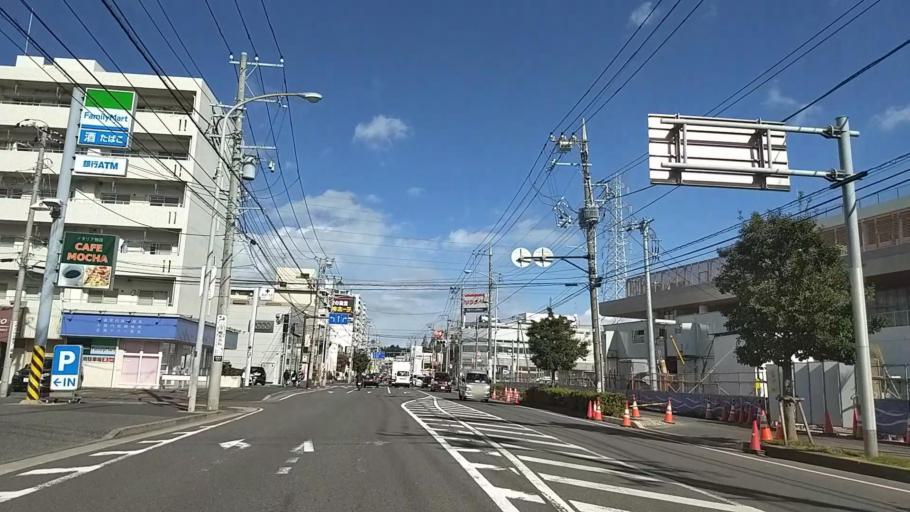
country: JP
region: Kanagawa
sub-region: Kawasaki-shi
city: Kawasaki
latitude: 35.5425
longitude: 139.6408
